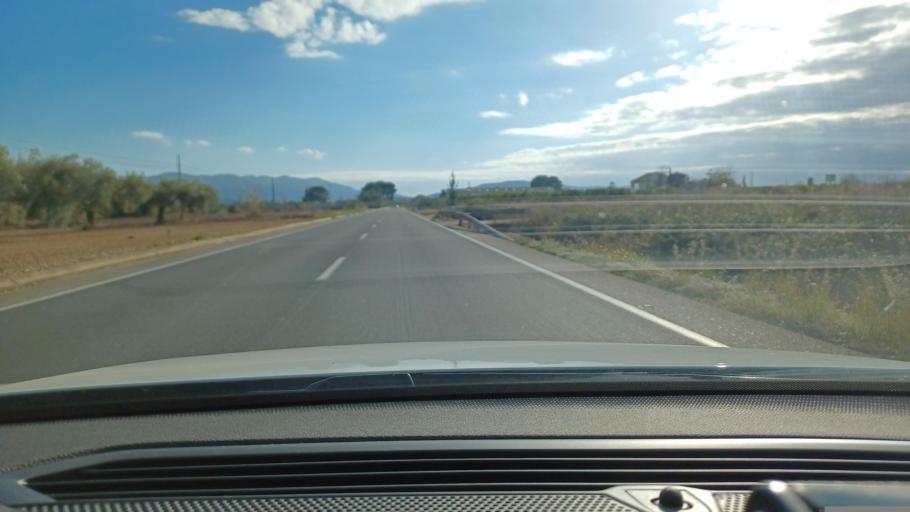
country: ES
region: Catalonia
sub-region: Provincia de Tarragona
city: Santa Barbara
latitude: 40.7301
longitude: 0.5032
